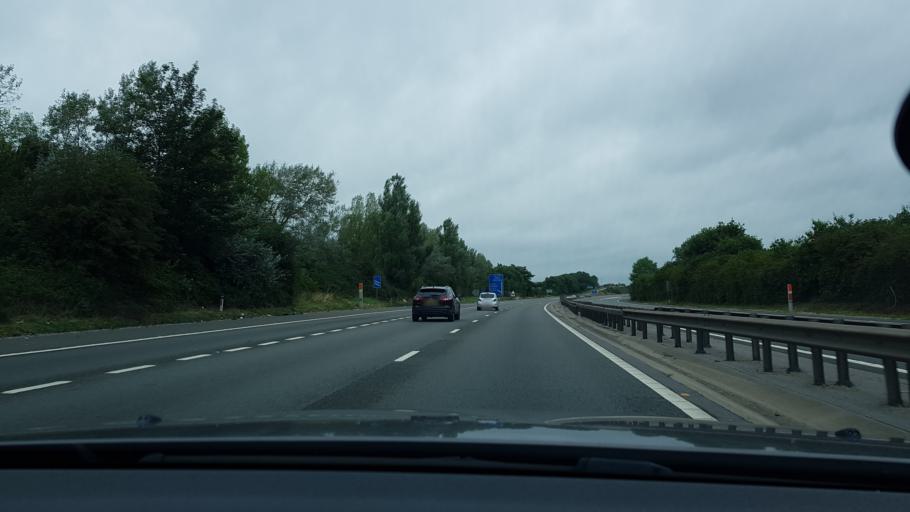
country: GB
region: England
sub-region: Hampshire
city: Totton
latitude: 50.9265
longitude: -1.4720
